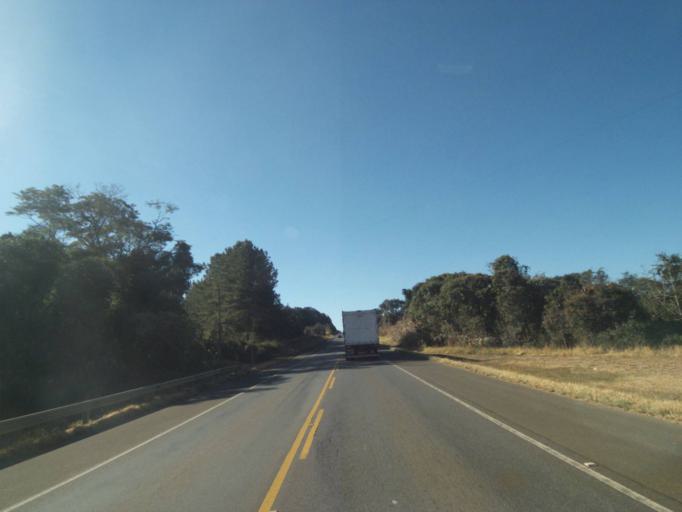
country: BR
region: Parana
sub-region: Tibagi
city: Tibagi
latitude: -24.5474
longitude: -50.4517
